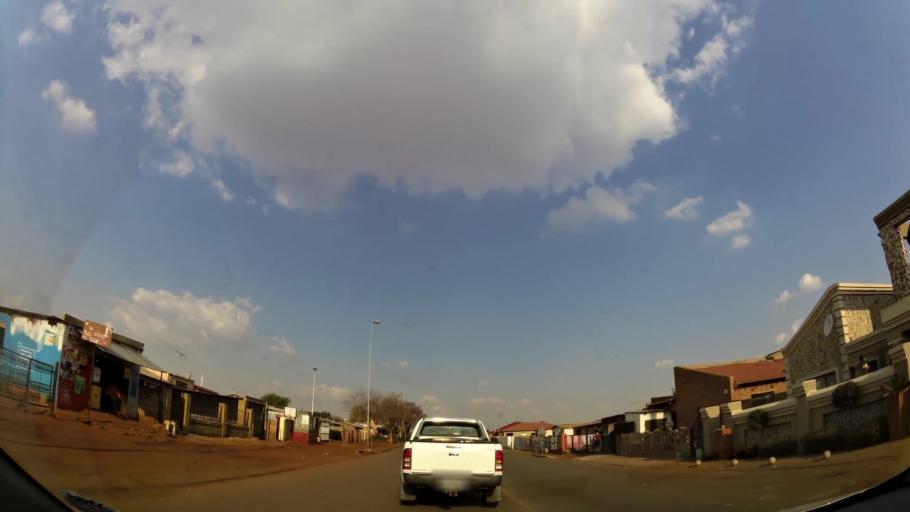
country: ZA
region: Gauteng
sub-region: Ekurhuleni Metropolitan Municipality
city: Germiston
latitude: -26.3549
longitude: 28.1896
